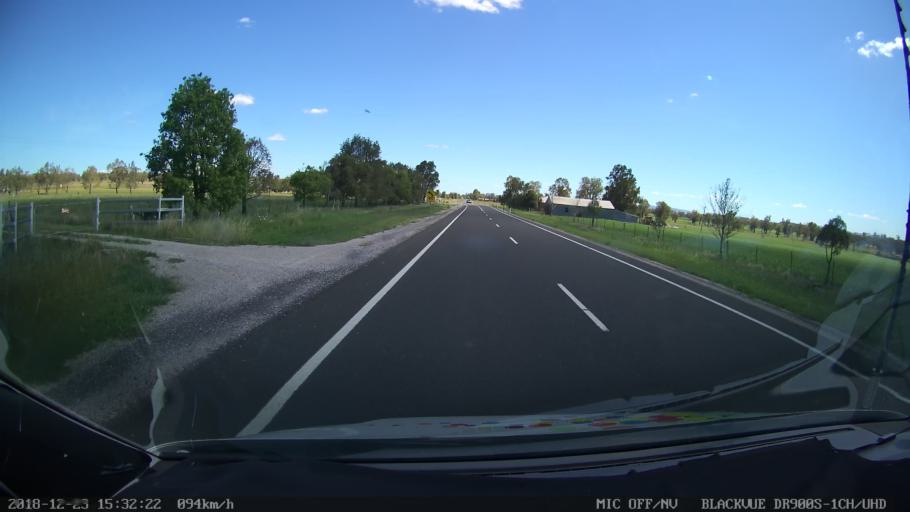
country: AU
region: New South Wales
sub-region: Tamworth Municipality
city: East Tamworth
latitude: -30.9846
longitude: 150.8702
